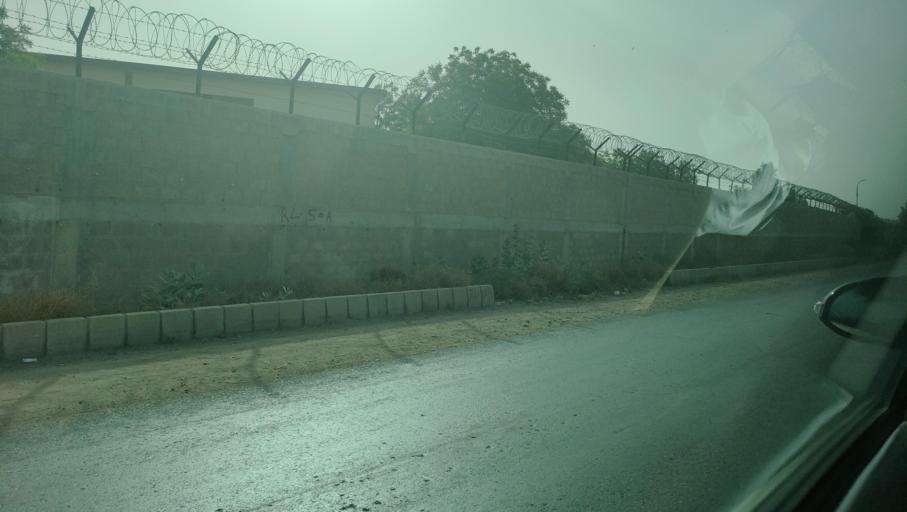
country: PK
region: Sindh
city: Malir Cantonment
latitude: 24.9165
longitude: 67.1879
